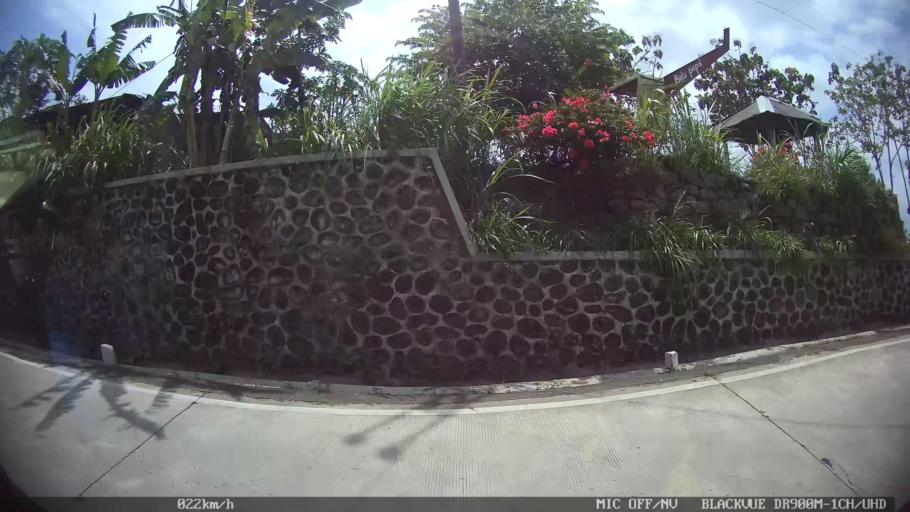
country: ID
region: Central Java
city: Candi Prambanan
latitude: -7.7896
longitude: 110.5184
